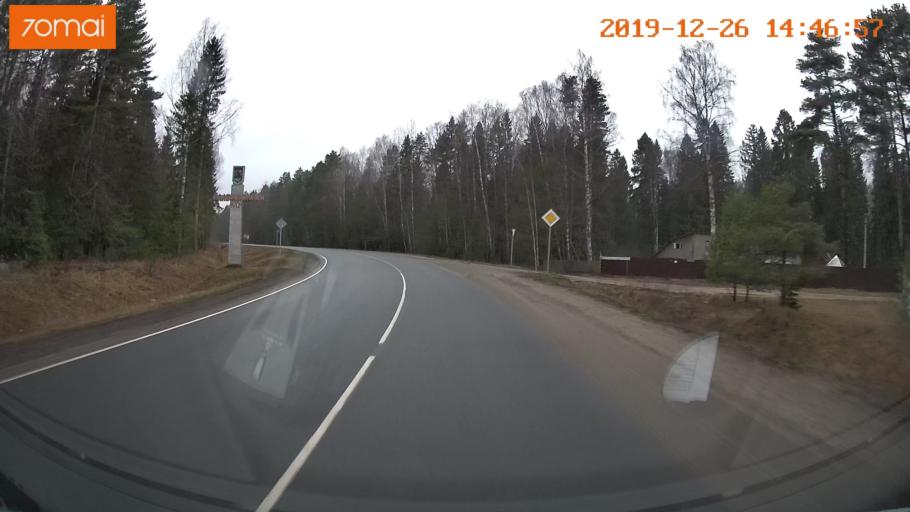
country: RU
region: Jaroslavl
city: Poshekhon'ye
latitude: 58.3410
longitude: 39.0090
